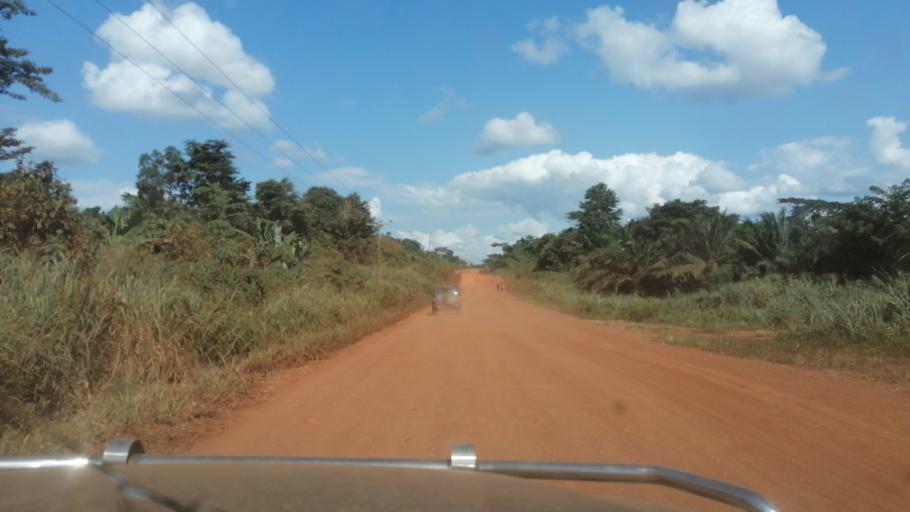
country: GH
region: Western
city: Bibiani
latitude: 6.6963
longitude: -2.5727
